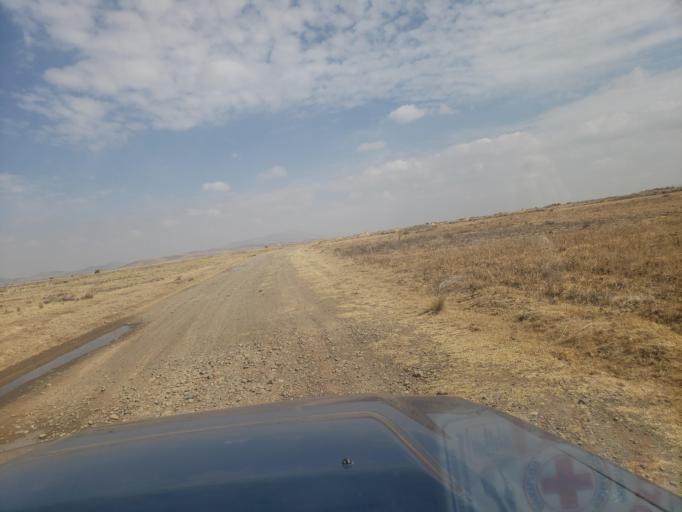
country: BO
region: La Paz
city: Batallas
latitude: -16.4165
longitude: -68.4239
